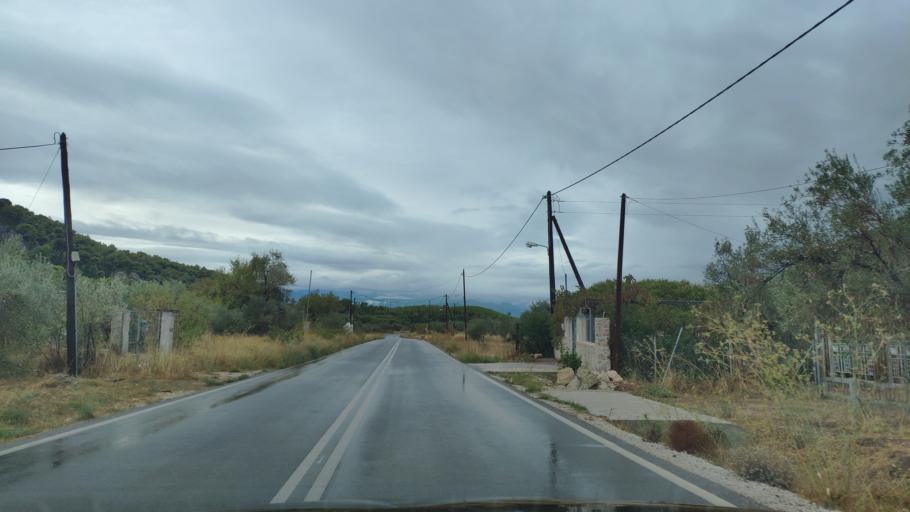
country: GR
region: Peloponnese
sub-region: Nomos Korinthias
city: Perachora
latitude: 38.0288
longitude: 22.9386
